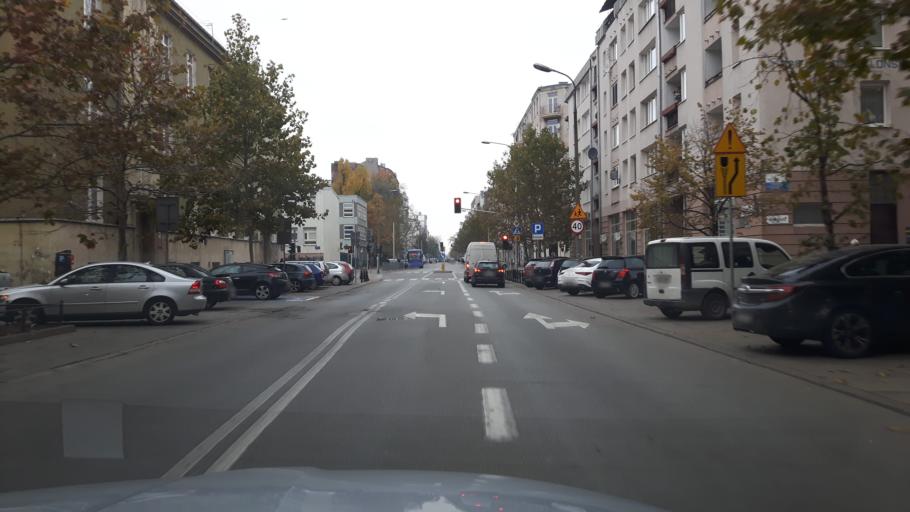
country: PL
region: Masovian Voivodeship
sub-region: Warszawa
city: Praga Polnoc
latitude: 52.2493
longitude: 21.0380
